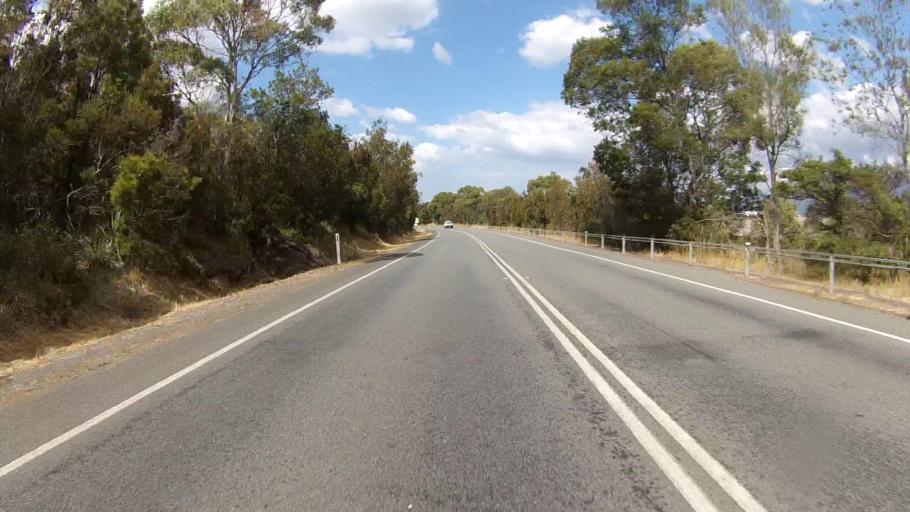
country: AU
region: Tasmania
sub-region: Brighton
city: Old Beach
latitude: -42.7751
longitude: 147.2695
